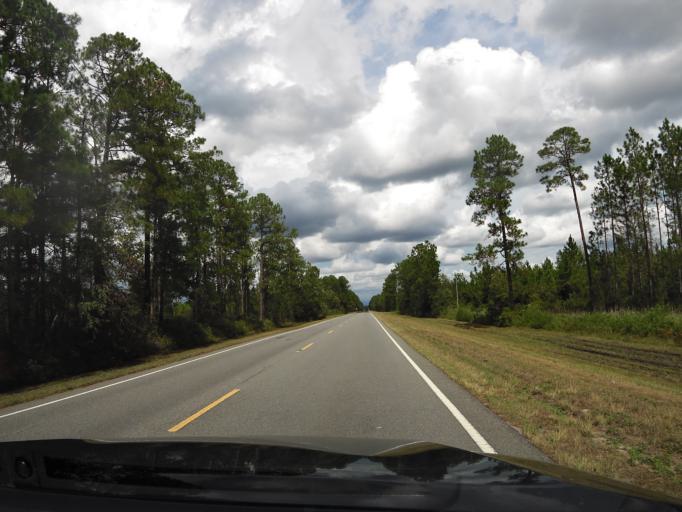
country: US
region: Georgia
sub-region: Brantley County
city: Nahunta
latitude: 31.1289
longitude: -81.9988
